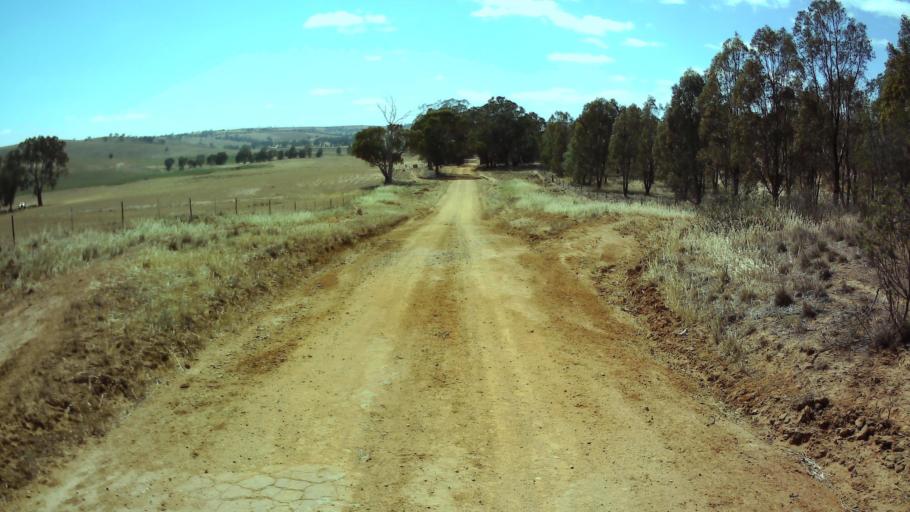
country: AU
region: New South Wales
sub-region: Weddin
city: Grenfell
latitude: -33.9543
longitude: 148.4093
